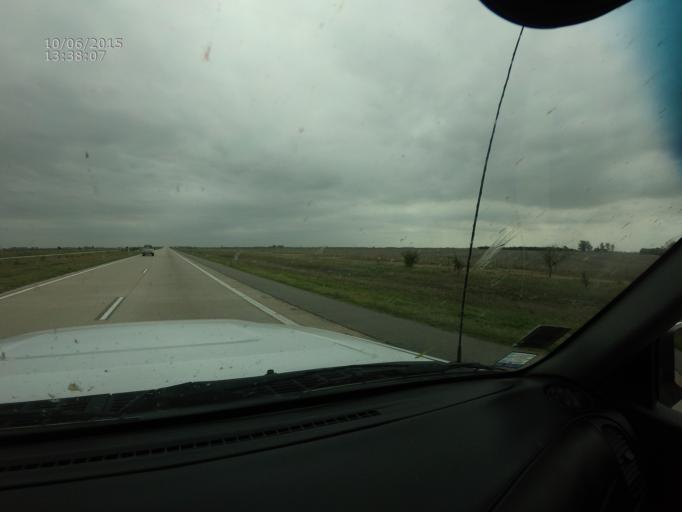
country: AR
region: Cordoba
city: Leones
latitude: -32.6055
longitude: -62.4284
